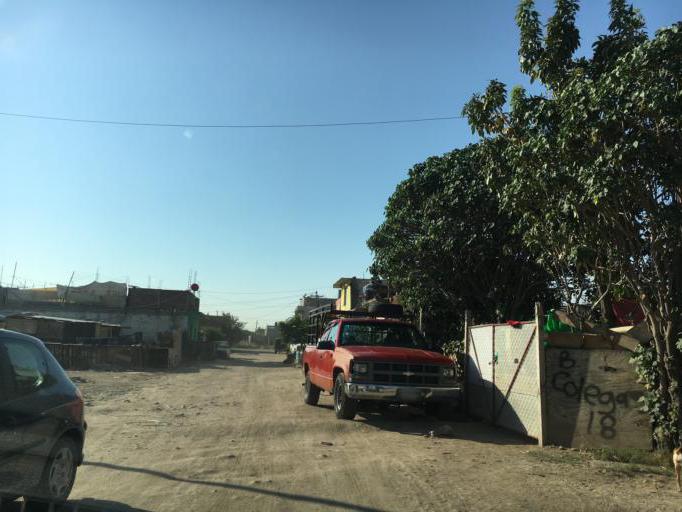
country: MX
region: Guanajuato
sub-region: Leon
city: Fraccionamiento Paraiso Real
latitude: 21.1039
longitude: -101.5974
